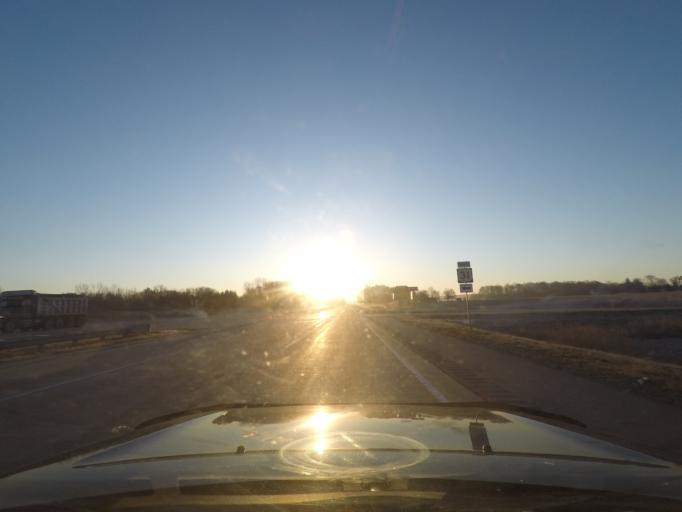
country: US
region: Indiana
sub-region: Marshall County
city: Plymouth
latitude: 41.4497
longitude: -86.2914
